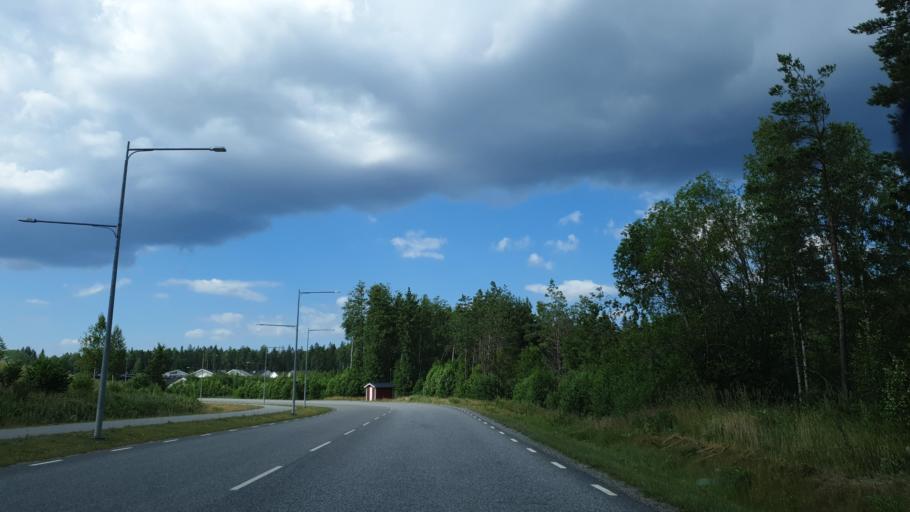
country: SE
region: Stockholm
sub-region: Sodertalje Kommun
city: Soedertaelje
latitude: 59.2179
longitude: 17.6512
